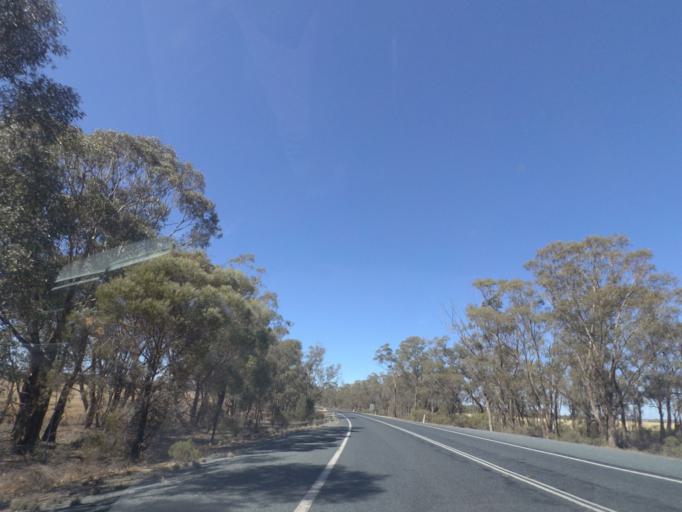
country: AU
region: New South Wales
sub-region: Bland
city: West Wyalong
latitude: -34.1191
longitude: 147.1285
